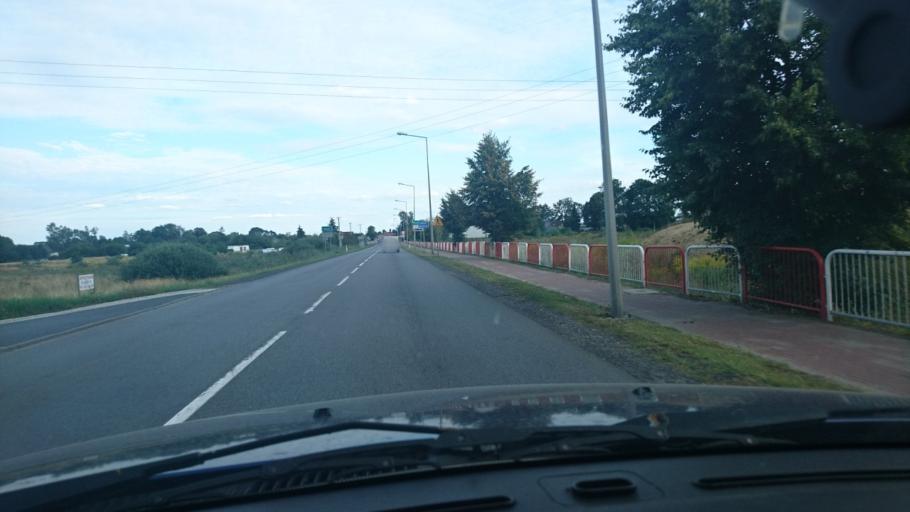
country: PL
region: Greater Poland Voivodeship
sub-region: Powiat kepinski
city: Kepno
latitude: 51.2712
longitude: 17.9940
